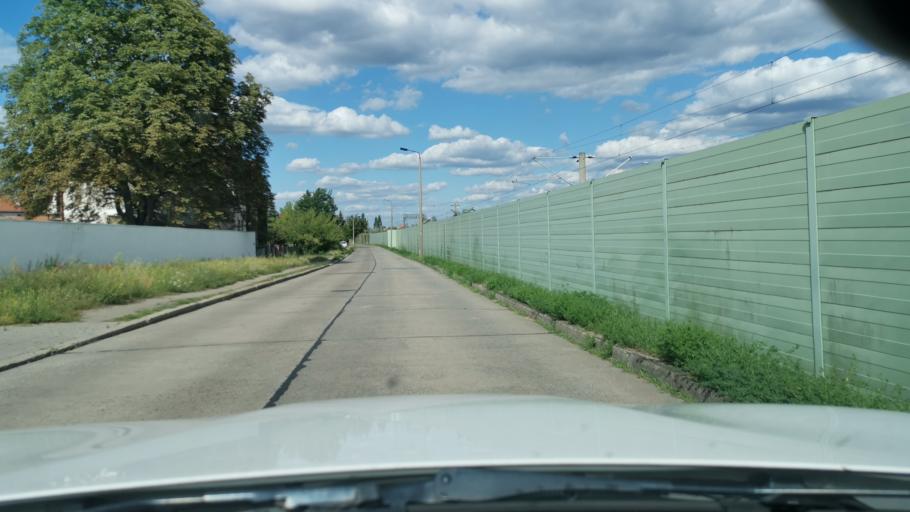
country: DE
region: Brandenburg
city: Luckenwalde
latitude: 52.0842
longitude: 13.1514
